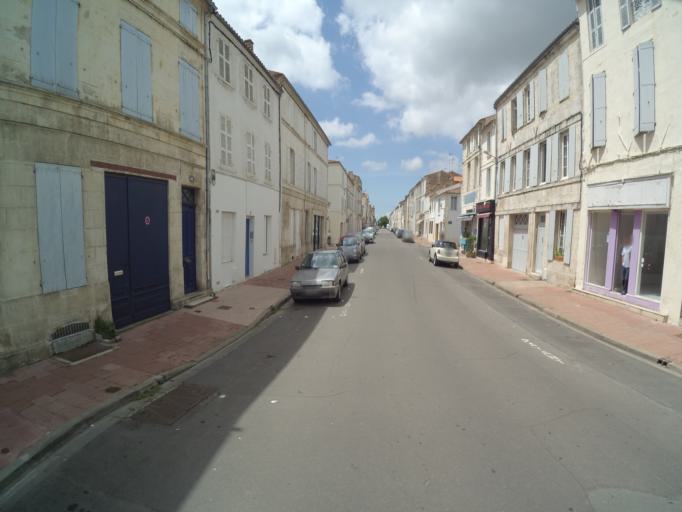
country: FR
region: Poitou-Charentes
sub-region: Departement de la Charente-Maritime
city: Rochefort
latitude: 45.9340
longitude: -0.9603
